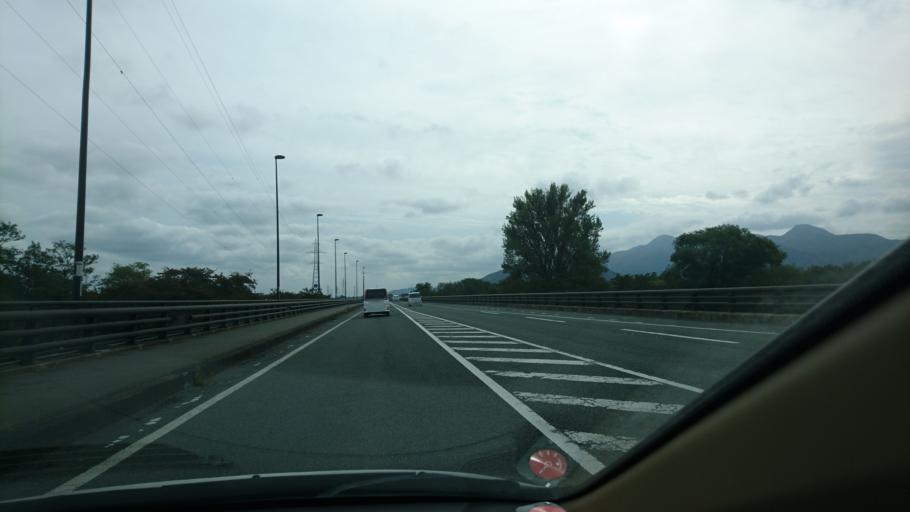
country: JP
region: Iwate
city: Morioka-shi
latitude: 39.7079
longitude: 141.1014
